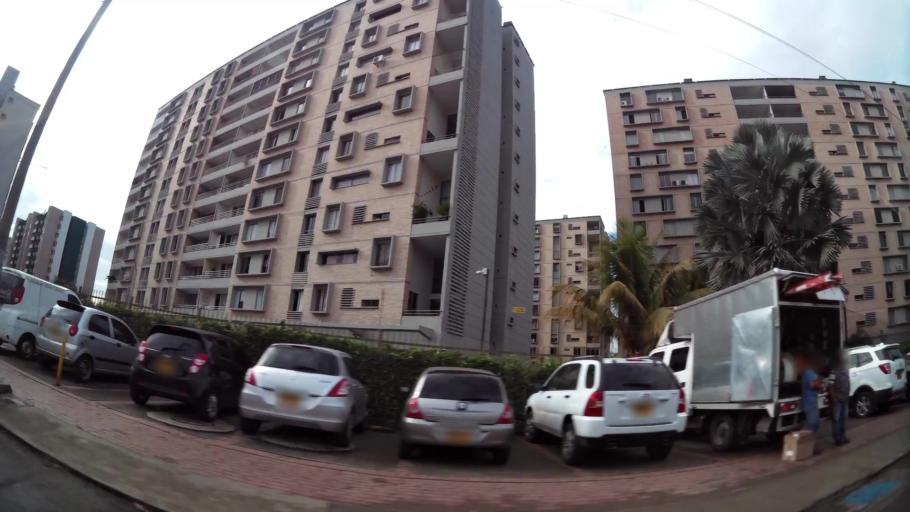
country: CO
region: Valle del Cauca
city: Cali
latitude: 3.4902
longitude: -76.5229
